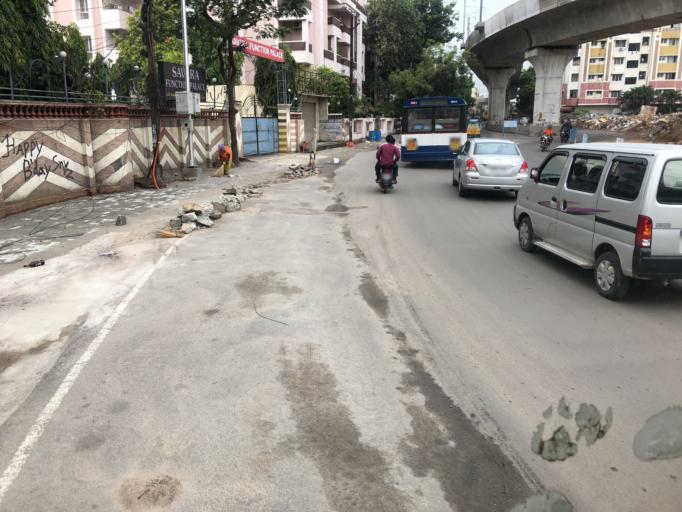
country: IN
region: Telangana
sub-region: Rangareddi
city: Kukatpalli
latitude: 17.4357
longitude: 78.4316
